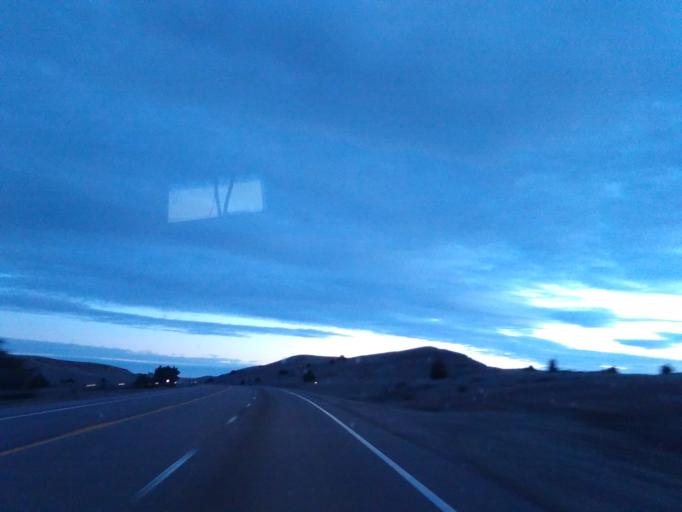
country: US
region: Nebraska
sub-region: Garden County
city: Oshkosh
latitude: 41.2538
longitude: -102.1053
